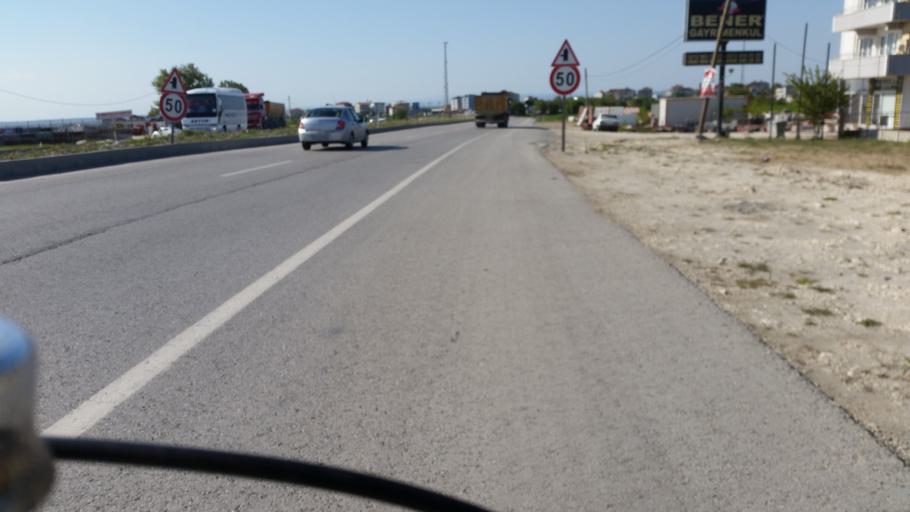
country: TR
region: Tekirdag
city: Cerkezkoey
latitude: 41.3511
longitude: 27.9575
